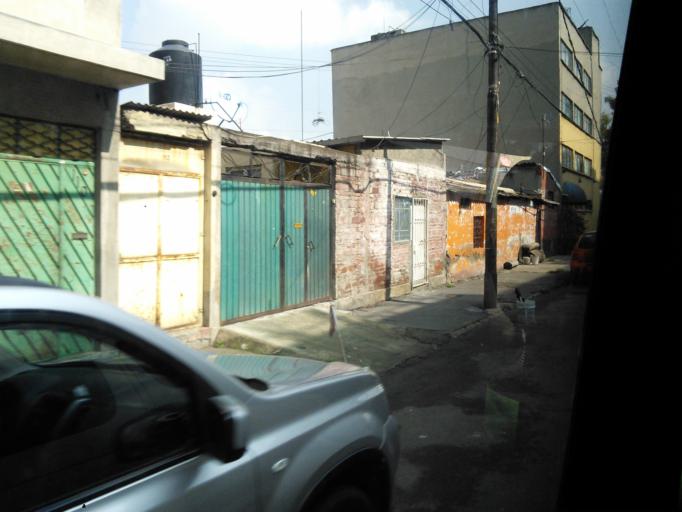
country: MX
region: Mexico City
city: Cuauhtemoc
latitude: 19.4660
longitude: -99.1398
